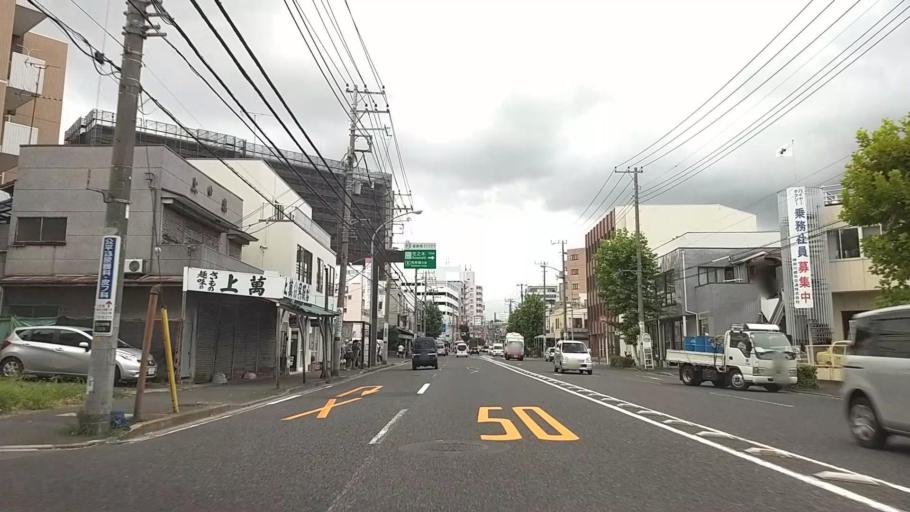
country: JP
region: Kanagawa
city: Yokohama
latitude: 35.4310
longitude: 139.6036
